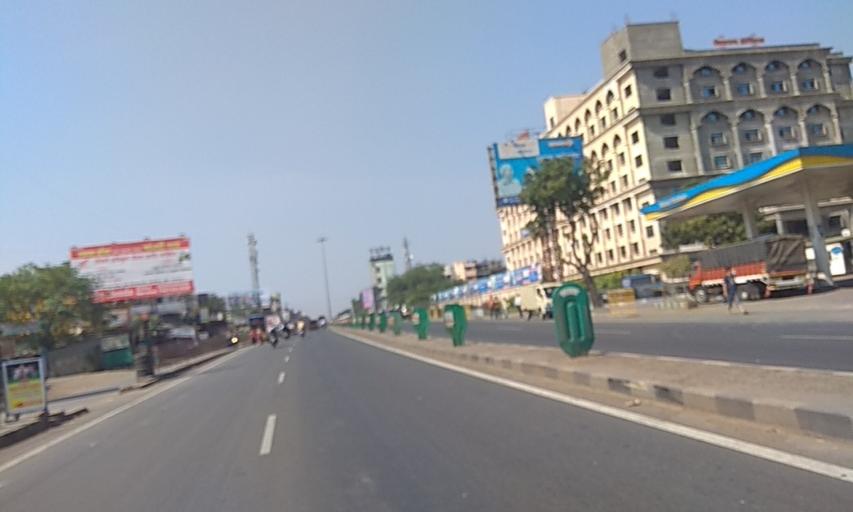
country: IN
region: Maharashtra
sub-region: Pune Division
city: Sasvad
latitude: 18.4889
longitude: 74.0236
